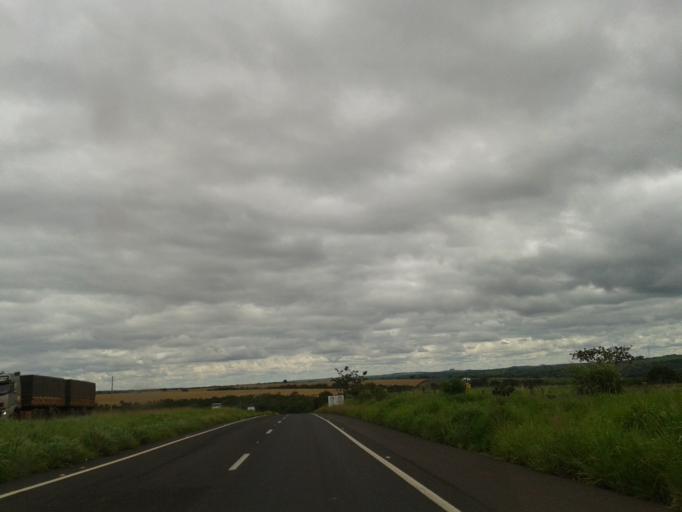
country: BR
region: Minas Gerais
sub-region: Monte Alegre De Minas
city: Monte Alegre de Minas
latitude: -18.8819
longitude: -49.0224
